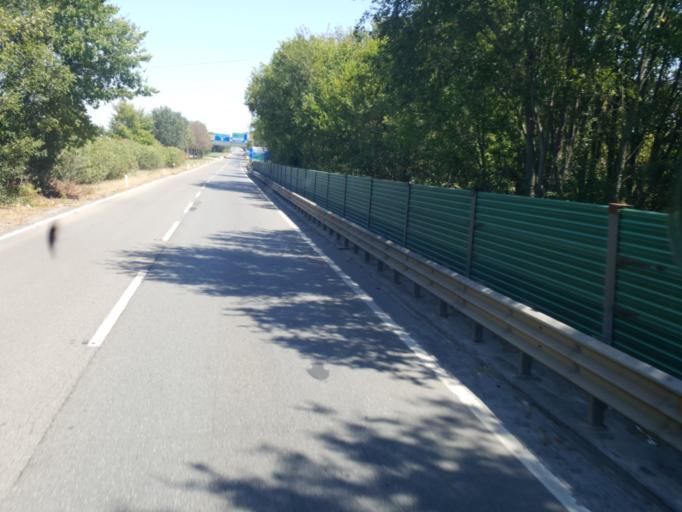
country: IT
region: Tuscany
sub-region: Provincia di Livorno
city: Guasticce
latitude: 43.5966
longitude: 10.3528
